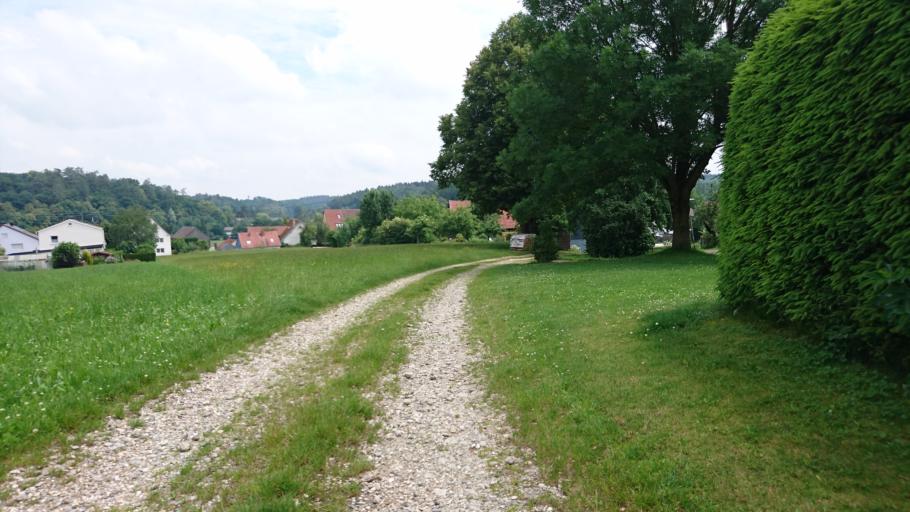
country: DE
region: Bavaria
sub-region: Swabia
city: Landensberg
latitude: 48.4334
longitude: 10.5029
